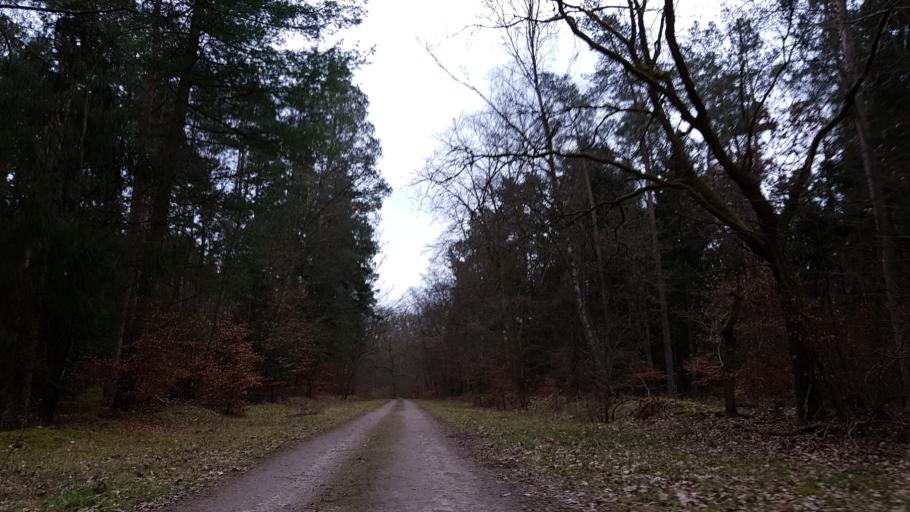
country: DE
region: Lower Saxony
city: Deutsch Evern
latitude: 53.2170
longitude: 10.4371
